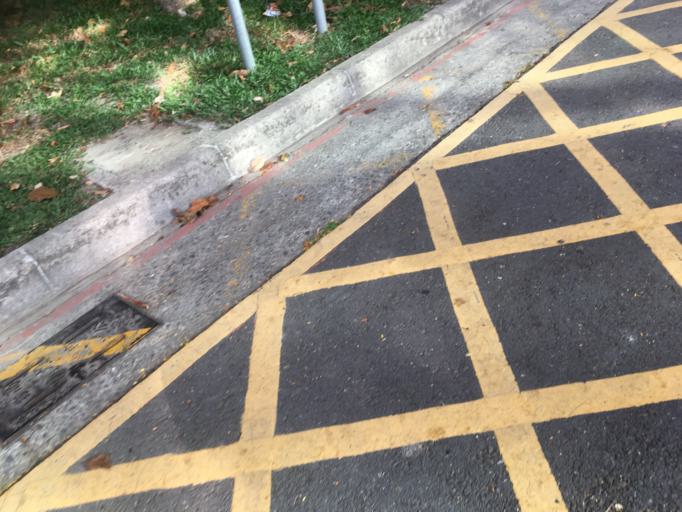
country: TW
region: Kaohsiung
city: Kaohsiung
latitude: 22.6229
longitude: 120.3223
